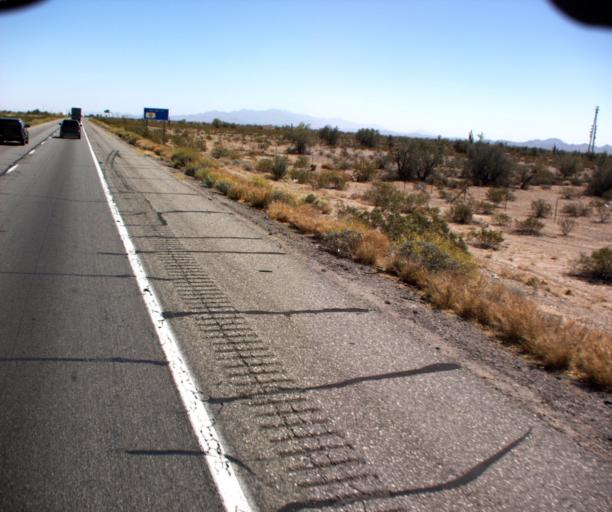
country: US
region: Arizona
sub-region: Maricopa County
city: Buckeye
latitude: 33.4305
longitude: -112.6409
